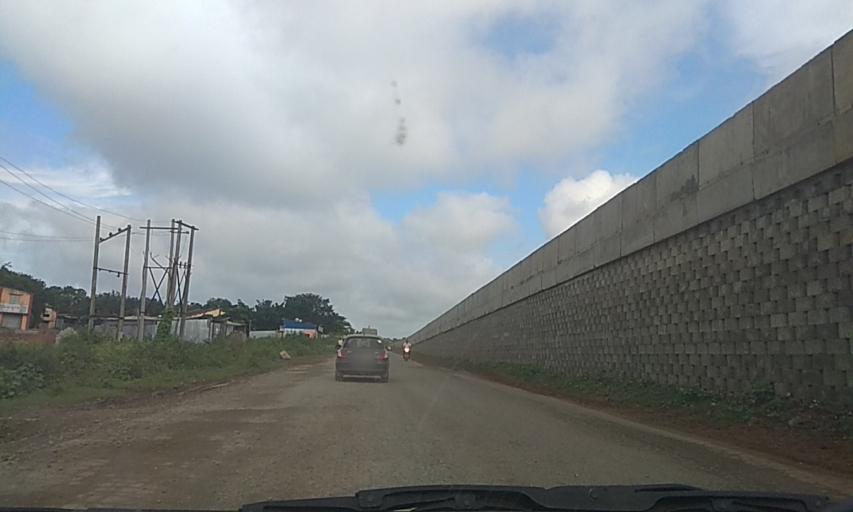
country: IN
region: Karnataka
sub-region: Haveri
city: Shiggaon
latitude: 14.9940
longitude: 75.2139
